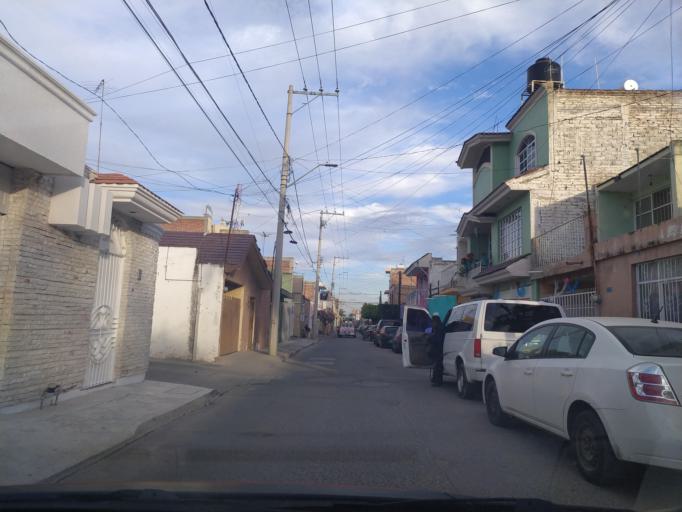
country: LA
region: Oudomxai
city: Muang La
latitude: 21.0314
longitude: 101.8806
